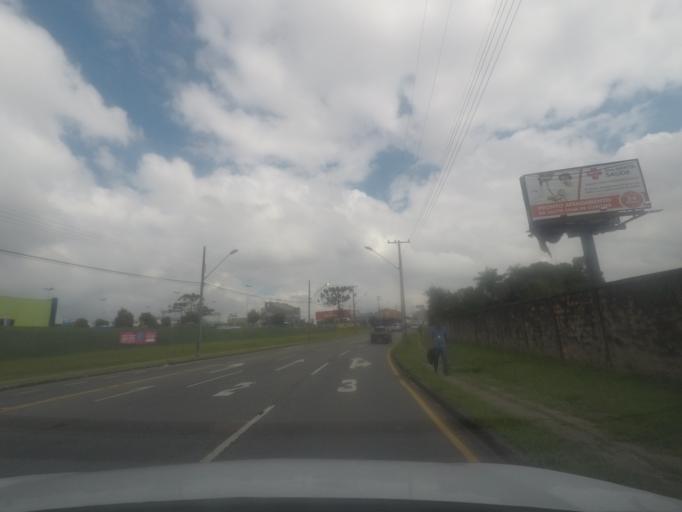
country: BR
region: Parana
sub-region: Curitiba
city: Curitiba
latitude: -25.4542
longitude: -49.2592
